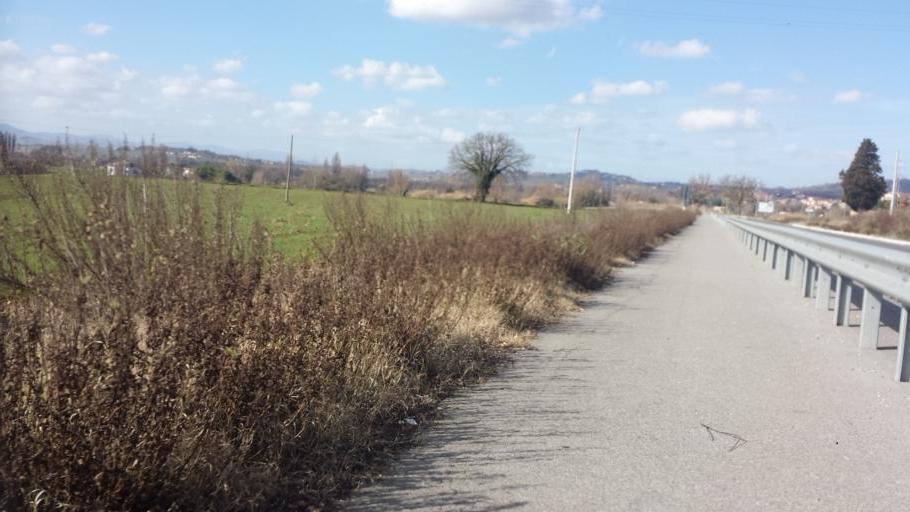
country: IT
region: Umbria
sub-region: Provincia di Terni
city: Terni
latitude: 42.5760
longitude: 12.5976
